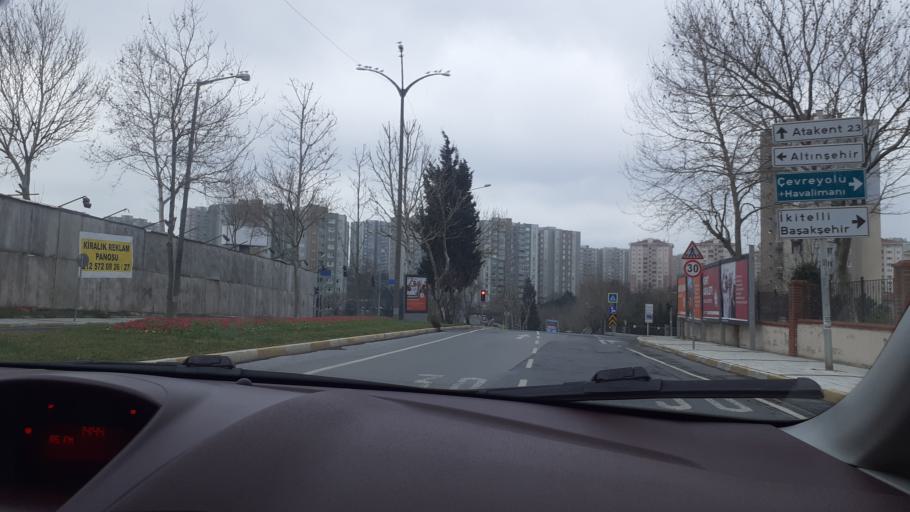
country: TR
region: Istanbul
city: Mahmutbey
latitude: 41.0481
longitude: 28.7872
